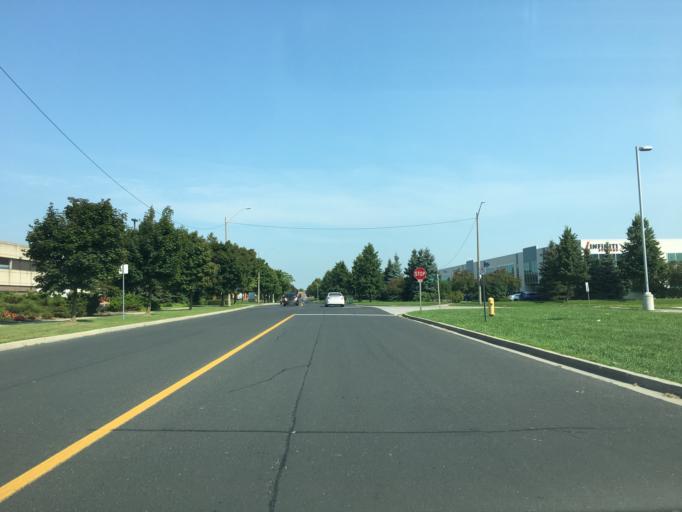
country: CA
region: Ontario
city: Markham
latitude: 43.8197
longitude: -79.3303
